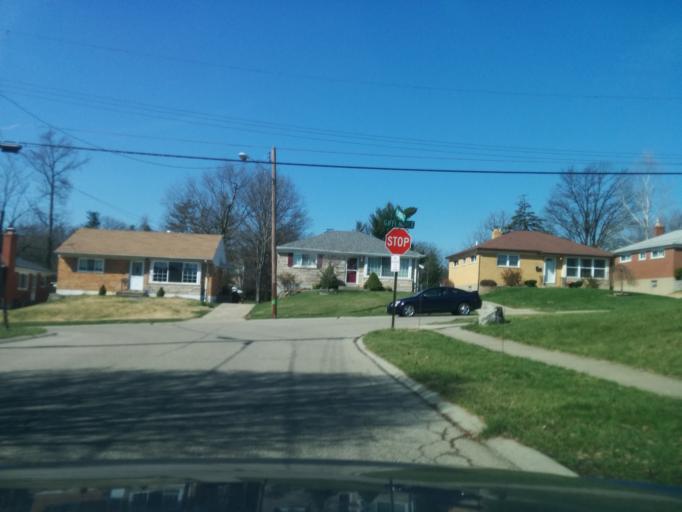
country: US
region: Ohio
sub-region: Hamilton County
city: Monfort Heights
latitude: 39.1997
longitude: -84.5916
